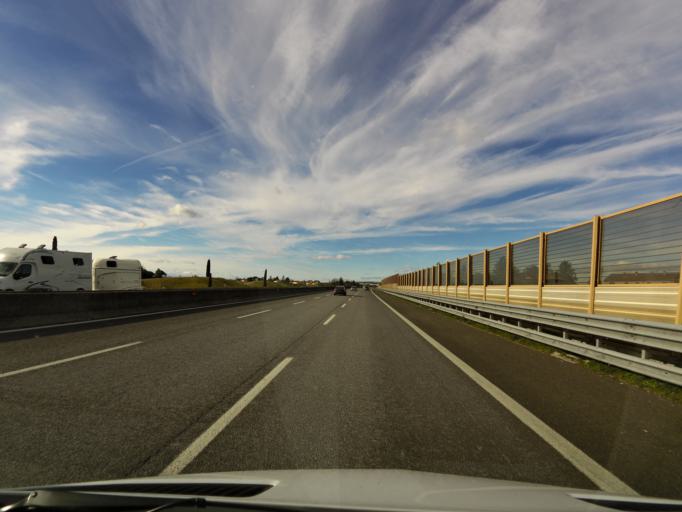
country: IT
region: Emilia-Romagna
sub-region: Forli-Cesena
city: Cesena
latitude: 44.1731
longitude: 12.2761
